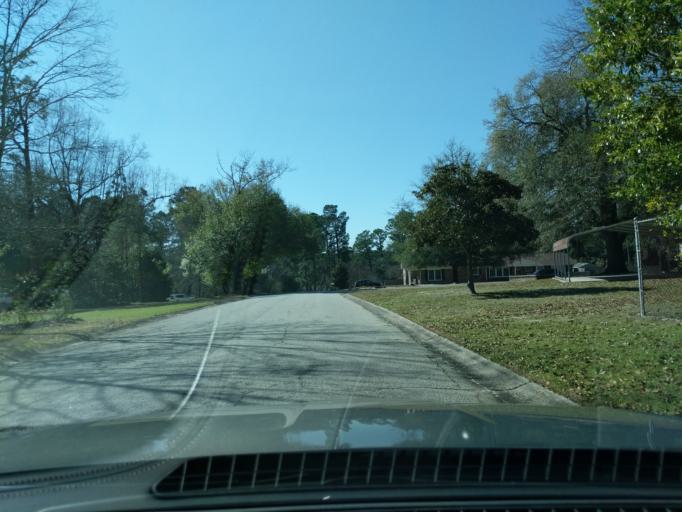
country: US
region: South Carolina
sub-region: Aiken County
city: Aiken
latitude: 33.5326
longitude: -81.7387
